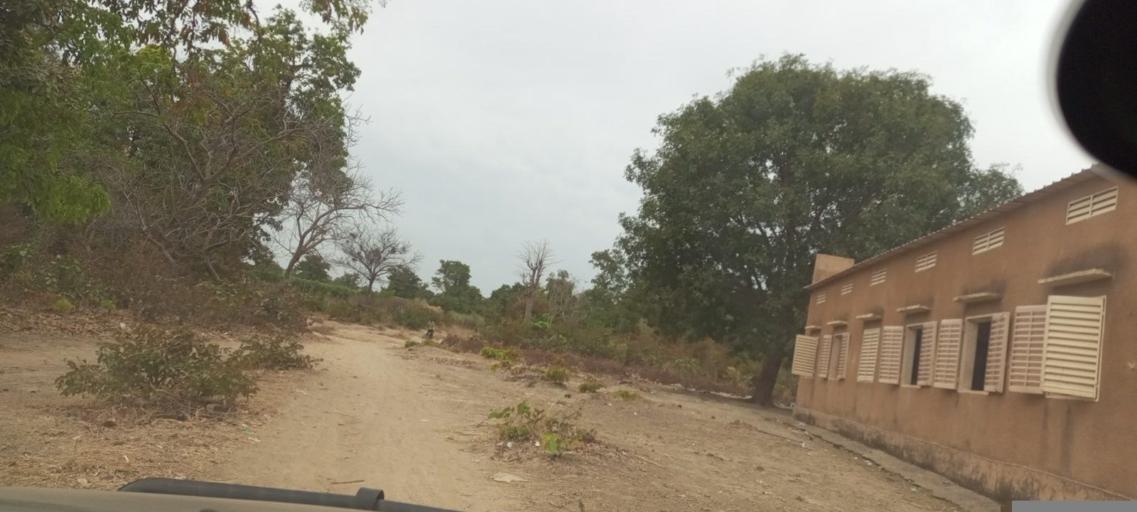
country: ML
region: Koulikoro
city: Kati
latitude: 12.7450
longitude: -8.3317
